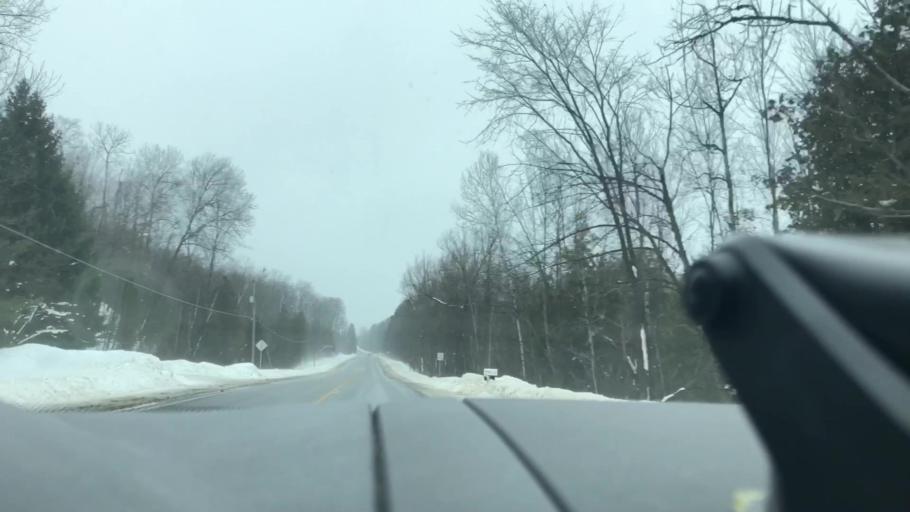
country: US
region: Michigan
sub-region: Charlevoix County
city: East Jordan
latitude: 45.1553
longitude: -85.1511
